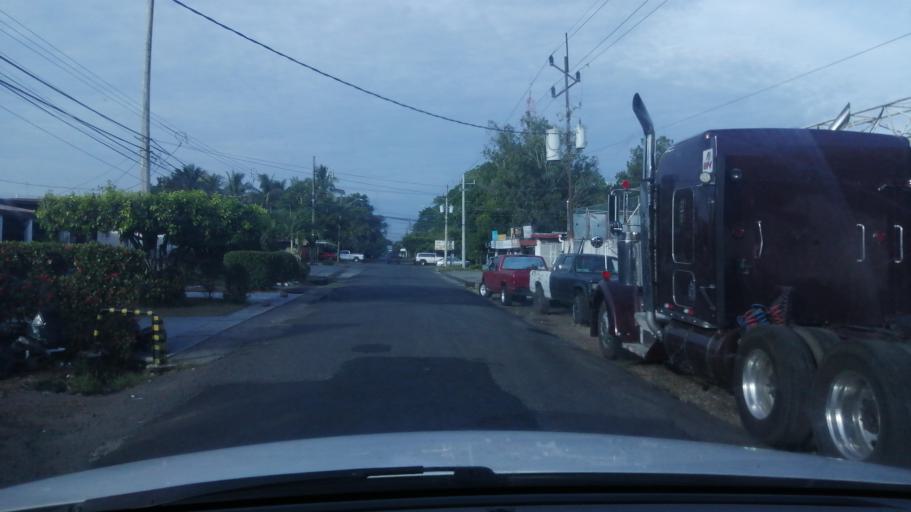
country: PA
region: Chiriqui
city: David
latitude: 8.4399
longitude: -82.4343
